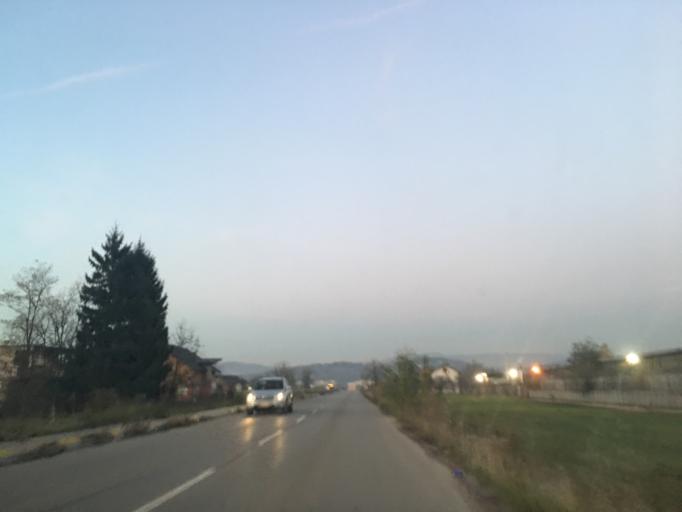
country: BA
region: Federation of Bosnia and Herzegovina
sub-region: Kanton Sarajevo
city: Sarajevo
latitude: 43.8148
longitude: 18.3408
